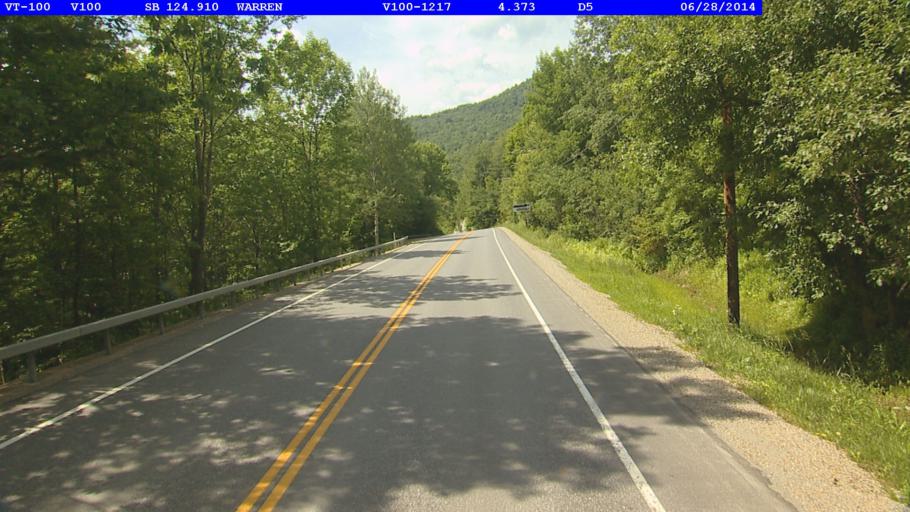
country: US
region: Vermont
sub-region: Washington County
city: Northfield
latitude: 44.1206
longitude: -72.8552
